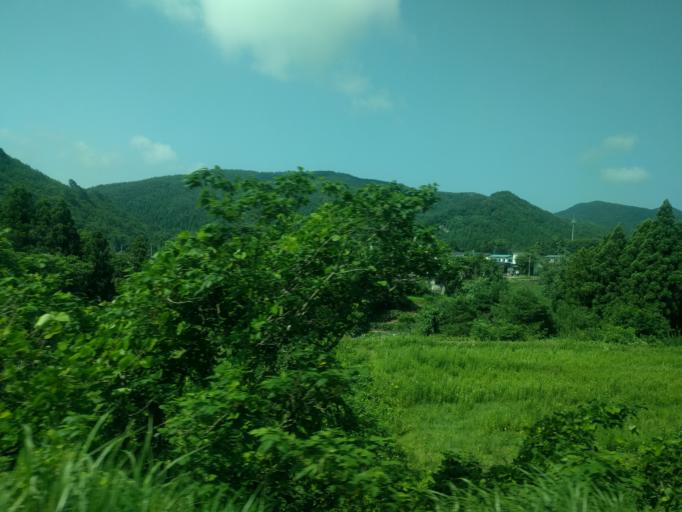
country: JP
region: Fukushima
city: Inawashiro
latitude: 37.4952
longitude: 140.2244
